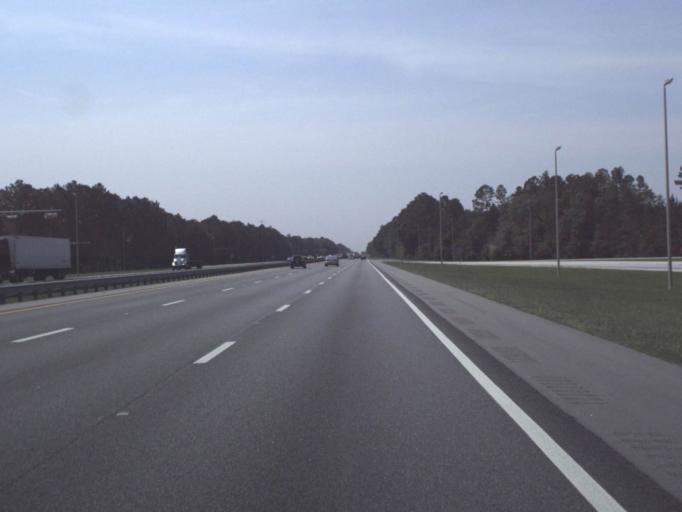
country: US
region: Florida
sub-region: Nassau County
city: Yulee
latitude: 30.6684
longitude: -81.6674
